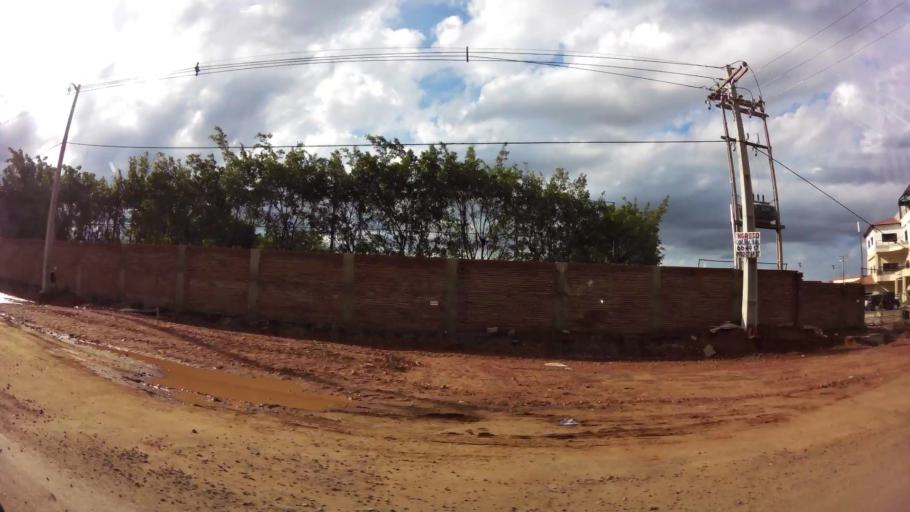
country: PY
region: Central
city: Fernando de la Mora
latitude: -25.2756
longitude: -57.5462
